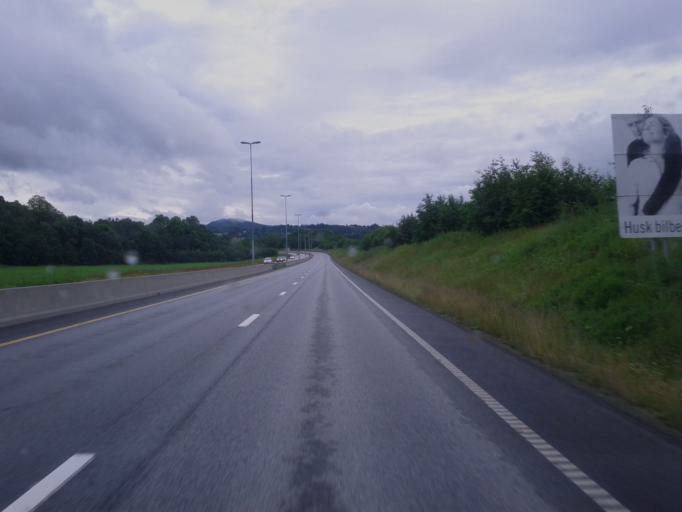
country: NO
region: Sor-Trondelag
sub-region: Melhus
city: Melhus
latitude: 63.2954
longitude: 10.2794
